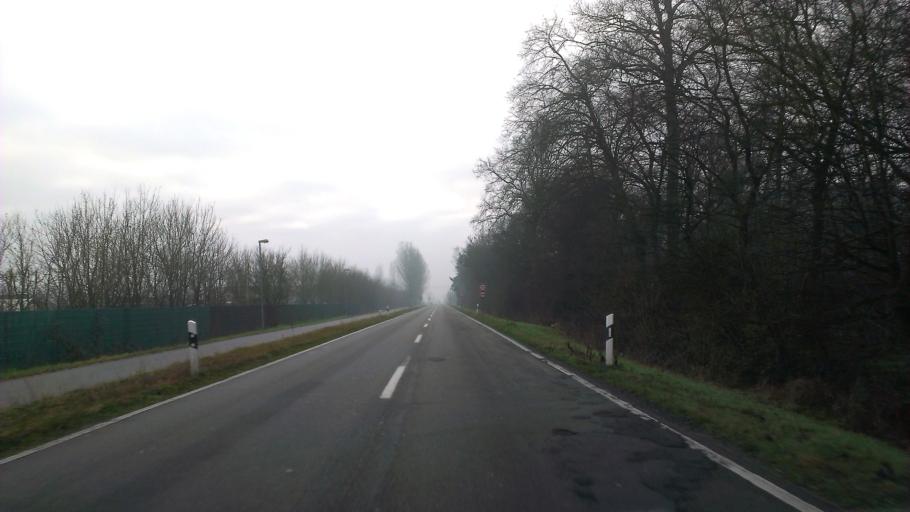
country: DE
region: Baden-Wuerttemberg
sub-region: Karlsruhe Region
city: Waghausel
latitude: 49.2290
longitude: 8.5309
